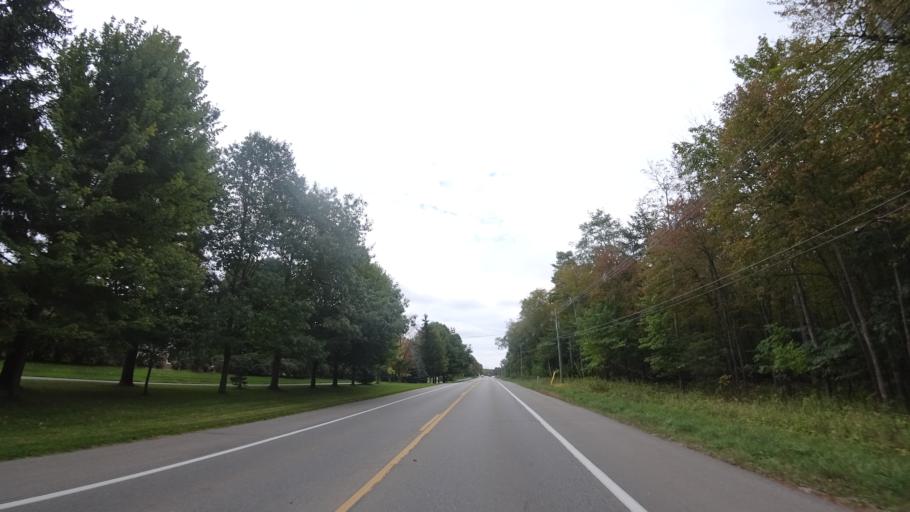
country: US
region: Michigan
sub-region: Emmet County
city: Harbor Springs
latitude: 45.4315
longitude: -84.9487
